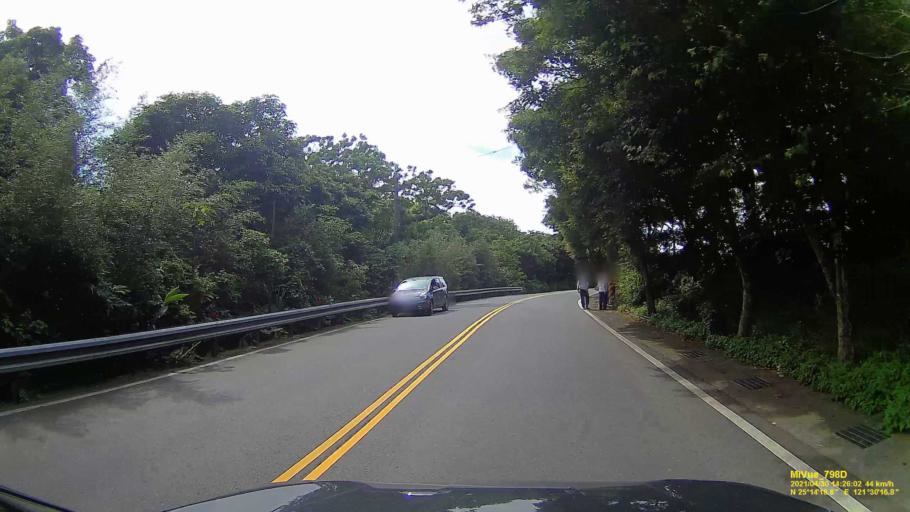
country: TW
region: Taipei
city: Taipei
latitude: 25.2381
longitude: 121.5044
